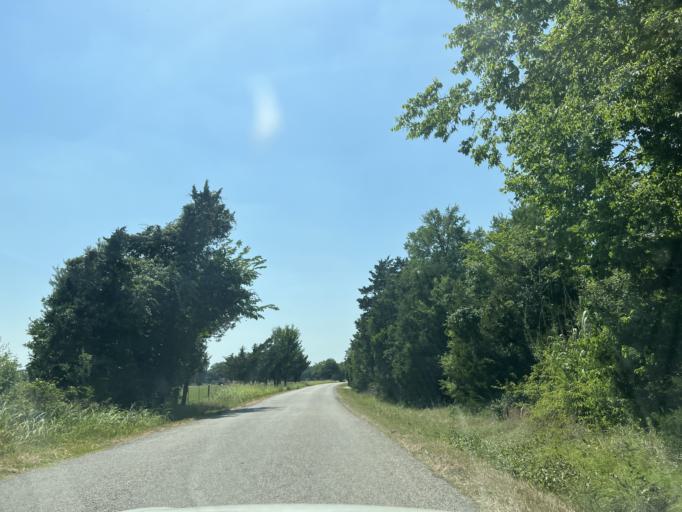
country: US
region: Texas
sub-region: Washington County
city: Brenham
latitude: 30.1541
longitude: -96.4875
